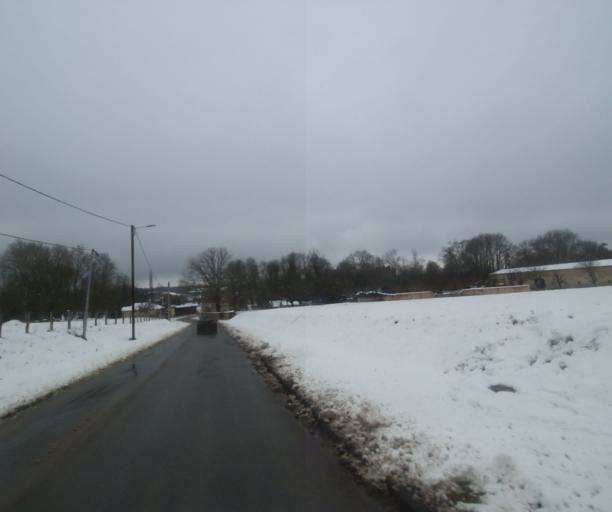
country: FR
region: Champagne-Ardenne
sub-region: Departement de la Haute-Marne
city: Laneuville-a-Remy
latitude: 48.4751
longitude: 4.8861
